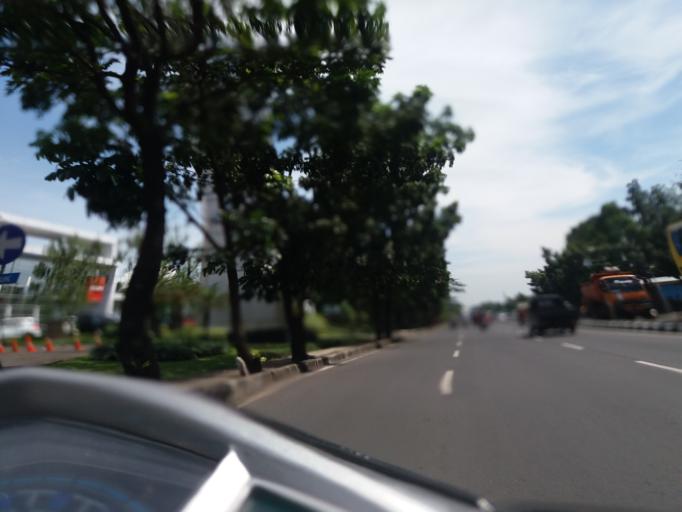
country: ID
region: West Java
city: Bandung
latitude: -6.9490
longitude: 107.6182
